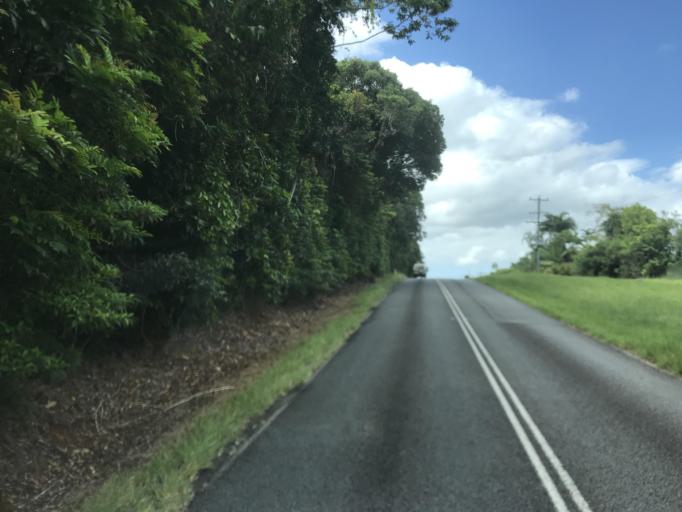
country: AU
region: Queensland
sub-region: Cassowary Coast
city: Innisfail
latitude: -17.8311
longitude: 146.0541
